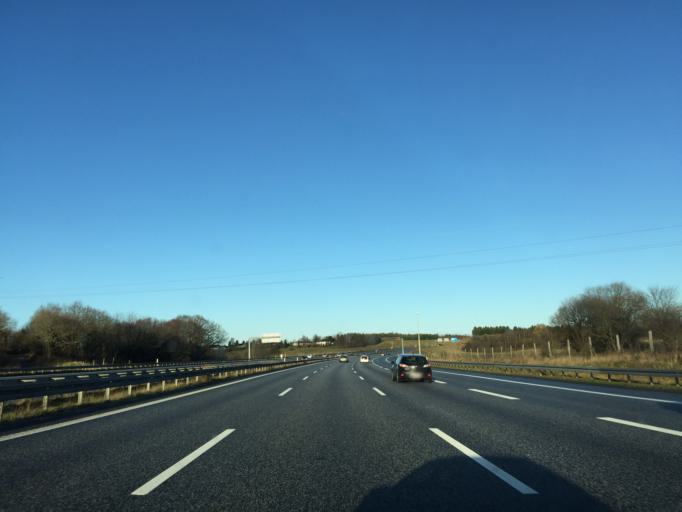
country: DK
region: South Denmark
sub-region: Vejle Kommune
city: Vejle
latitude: 55.6697
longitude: 9.5536
